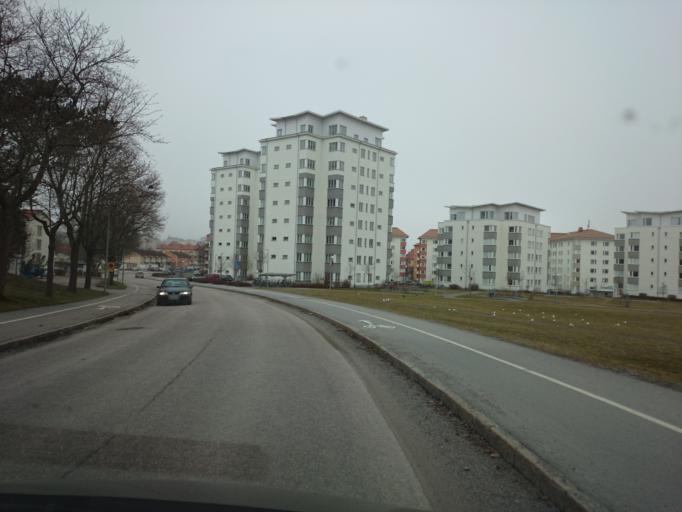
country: SE
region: Uppsala
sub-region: Uppsala Kommun
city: Uppsala
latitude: 59.8581
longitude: 17.6186
